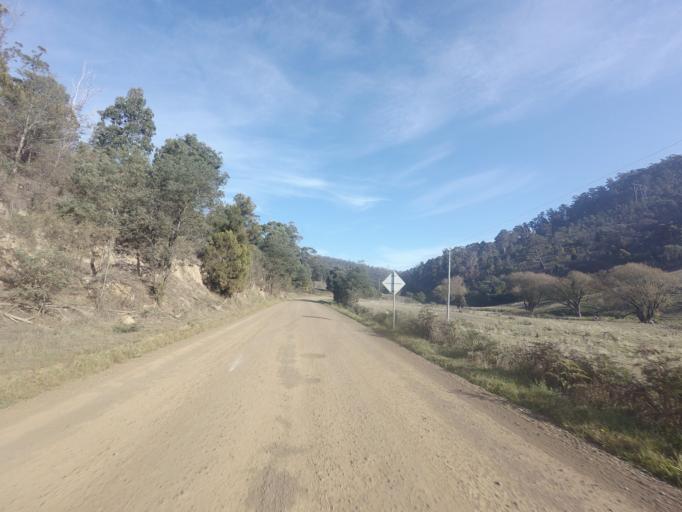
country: AU
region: Tasmania
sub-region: Sorell
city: Sorell
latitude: -42.5045
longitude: 147.4300
